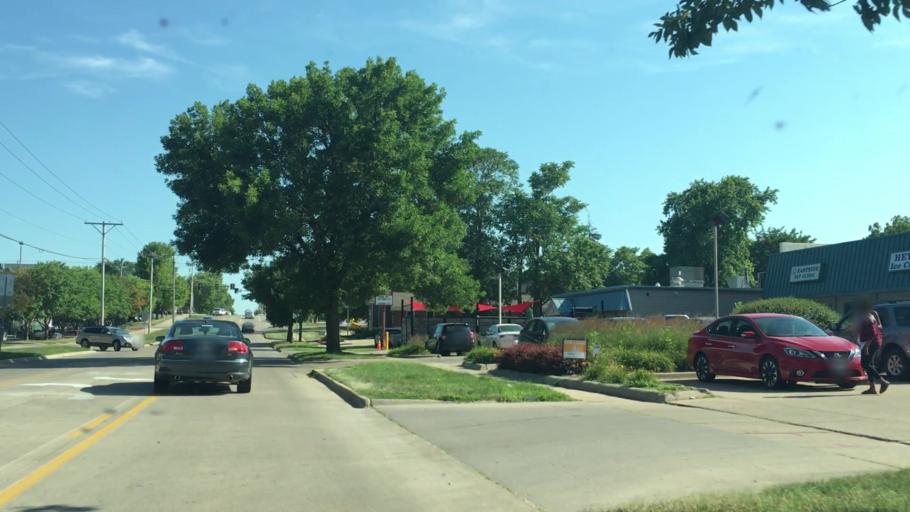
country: US
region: Iowa
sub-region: Johnson County
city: Iowa City
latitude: 41.6516
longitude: -91.5020
